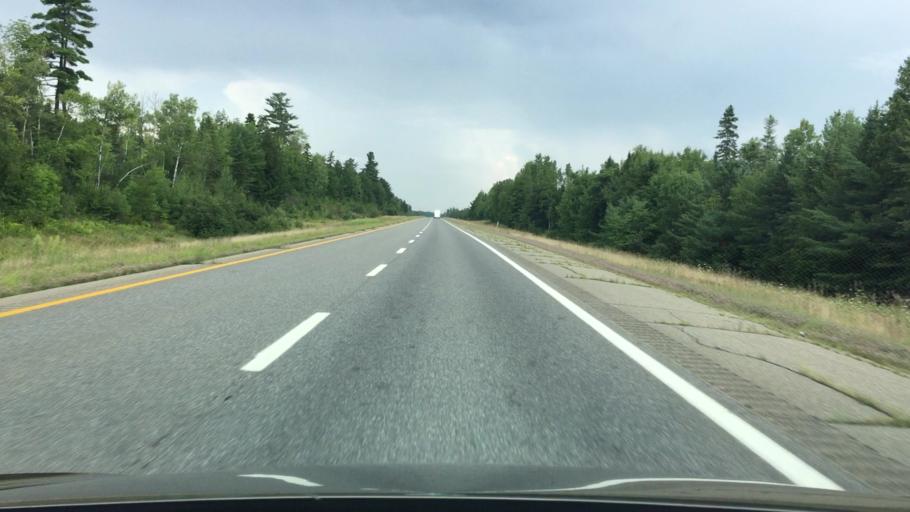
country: US
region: Maine
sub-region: Penobscot County
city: Medway
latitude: 45.5148
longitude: -68.5524
